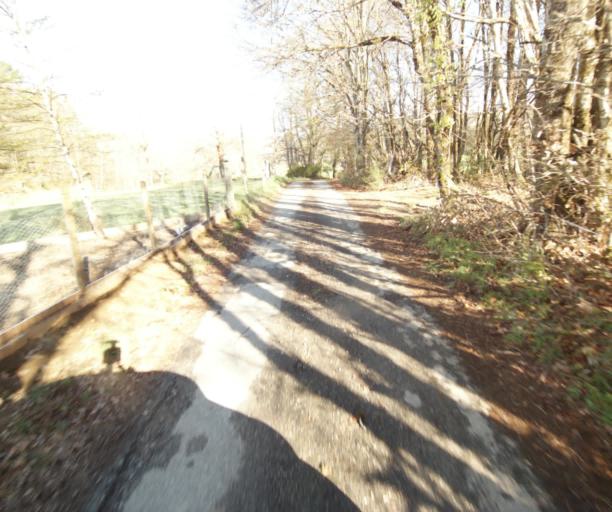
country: FR
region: Limousin
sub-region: Departement de la Correze
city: Laguenne
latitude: 45.2689
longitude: 1.8566
